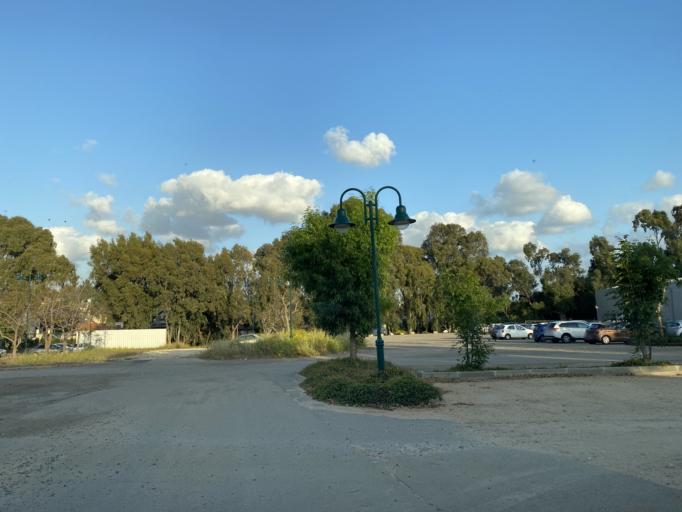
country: IL
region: Tel Aviv
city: Herzliyya
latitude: 32.1579
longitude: 34.8333
